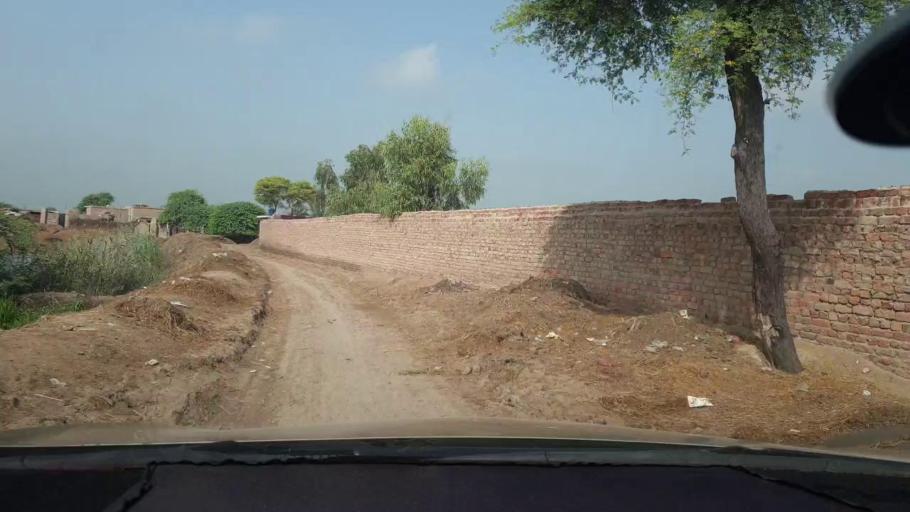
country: PK
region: Sindh
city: Kambar
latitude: 27.5416
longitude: 68.0483
